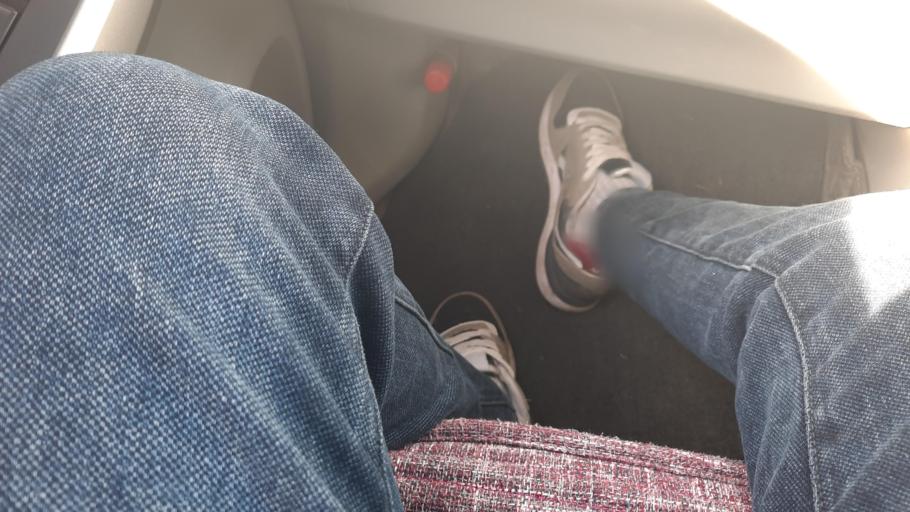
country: MN
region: Orhon
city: Erdenet
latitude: 49.0324
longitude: 104.0538
